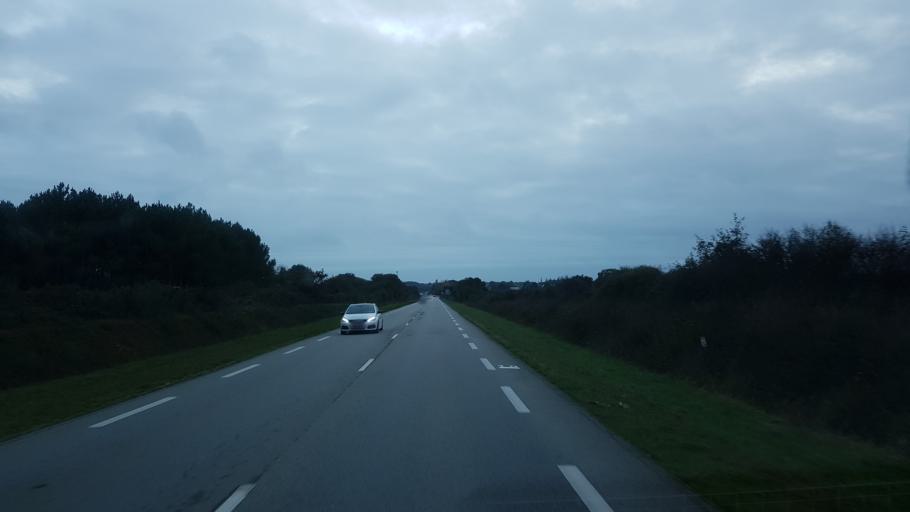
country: FR
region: Brittany
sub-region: Departement du Morbihan
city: Sarzeau
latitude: 47.5572
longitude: -2.7138
